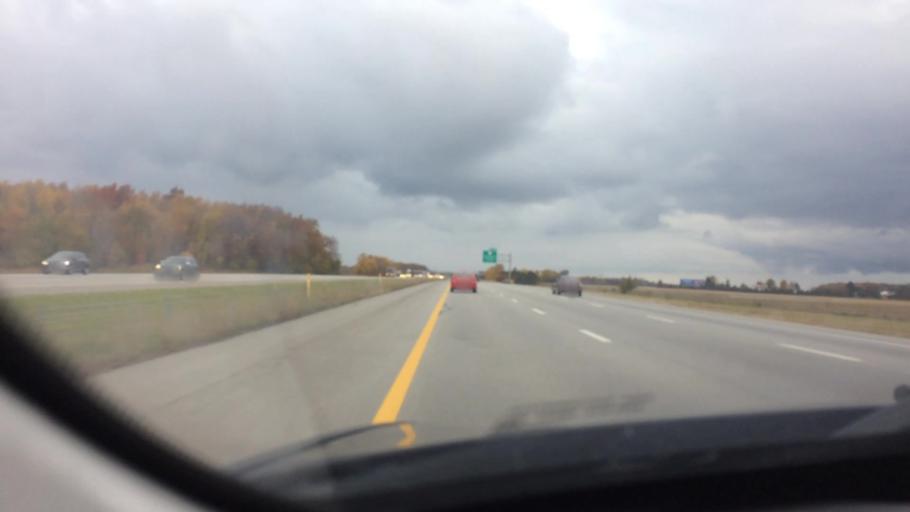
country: US
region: Ohio
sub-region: Wood County
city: Bowling Green
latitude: 41.3163
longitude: -83.6263
